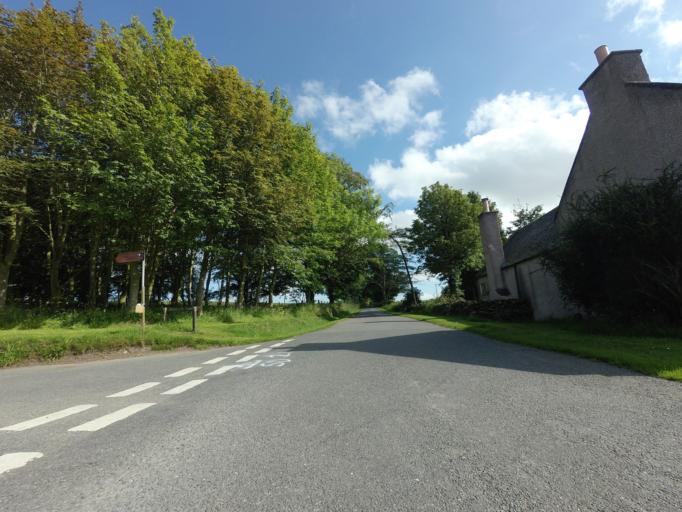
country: GB
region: Scotland
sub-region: Aberdeenshire
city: Turriff
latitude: 57.5931
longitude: -2.5076
